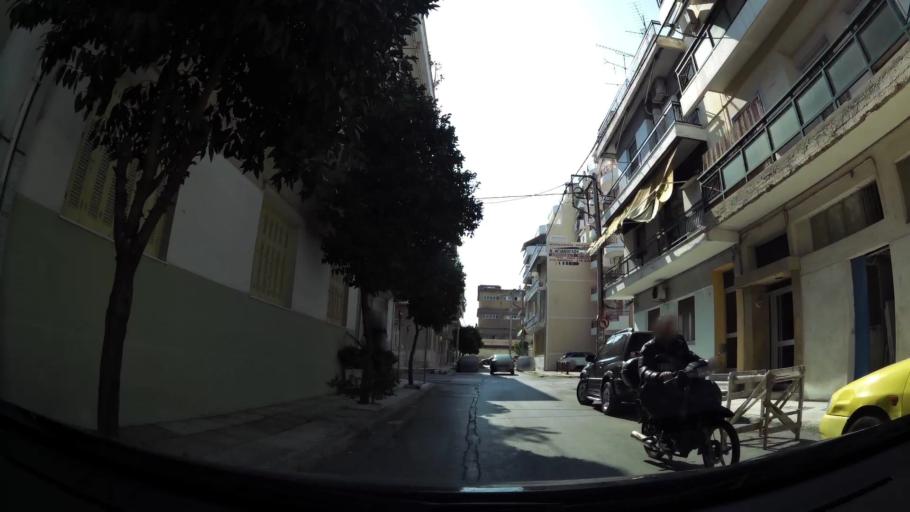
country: GR
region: Attica
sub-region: Nomos Piraios
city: Drapetsona
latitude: 37.9538
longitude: 23.6285
